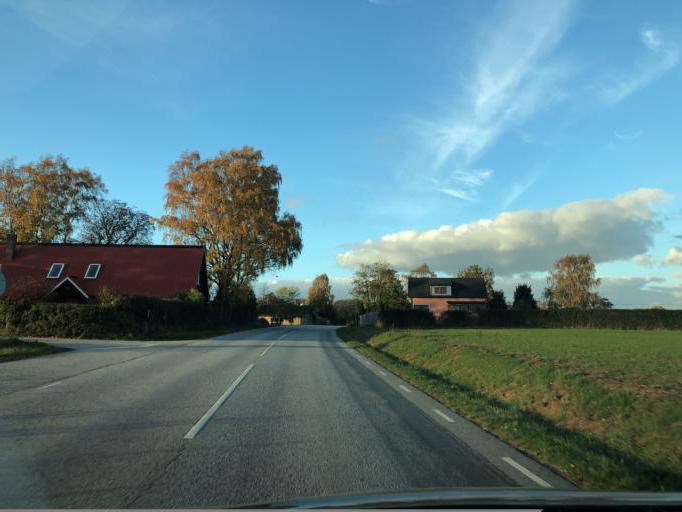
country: SE
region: Skane
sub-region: Kavlinge Kommun
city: Kaevlinge
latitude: 55.8110
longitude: 13.0920
